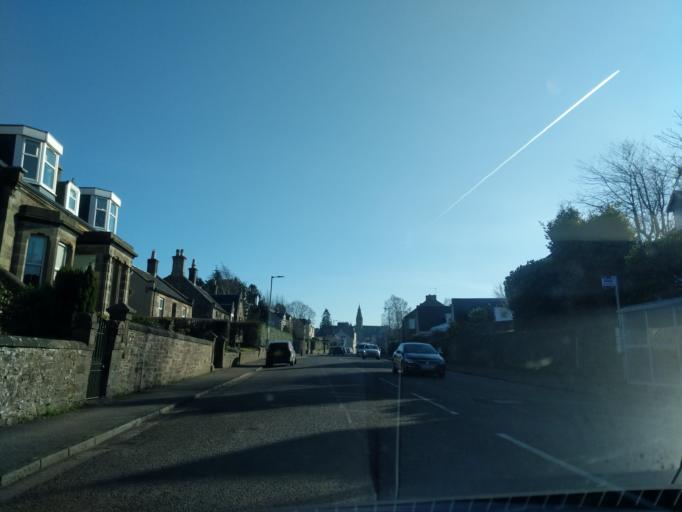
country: GB
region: Scotland
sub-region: South Lanarkshire
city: Lanark
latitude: 55.6756
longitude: -3.7872
